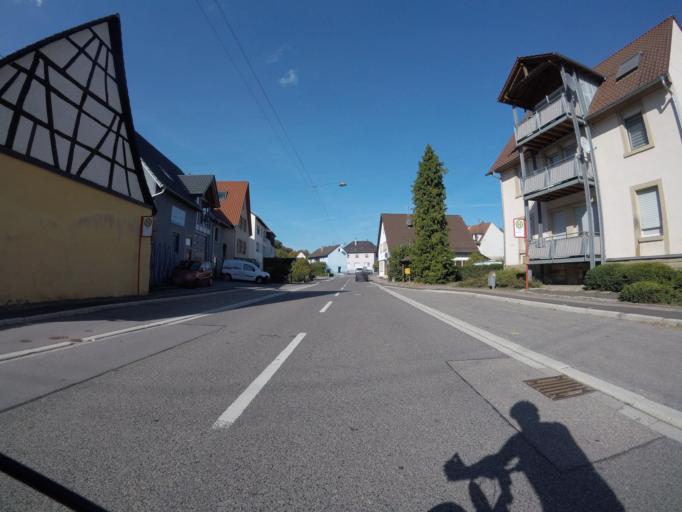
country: DE
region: Baden-Wuerttemberg
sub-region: Karlsruhe Region
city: Bretten
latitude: 49.0077
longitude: 8.7242
